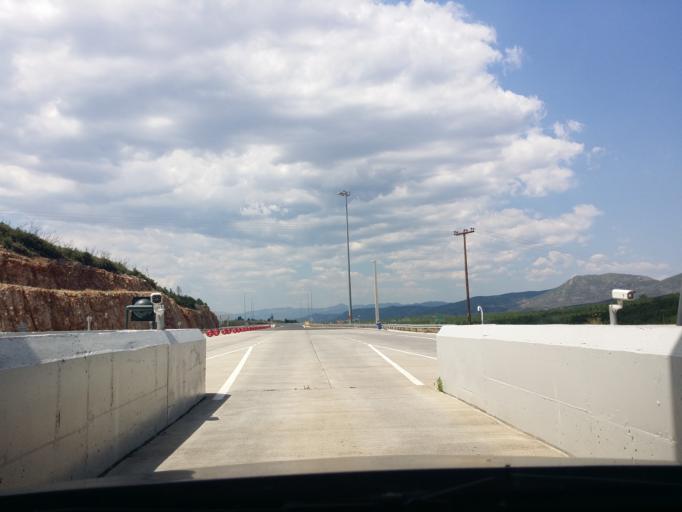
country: GR
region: Peloponnese
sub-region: Nomos Arkadias
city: Megalopoli
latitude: 37.2985
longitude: 22.2105
